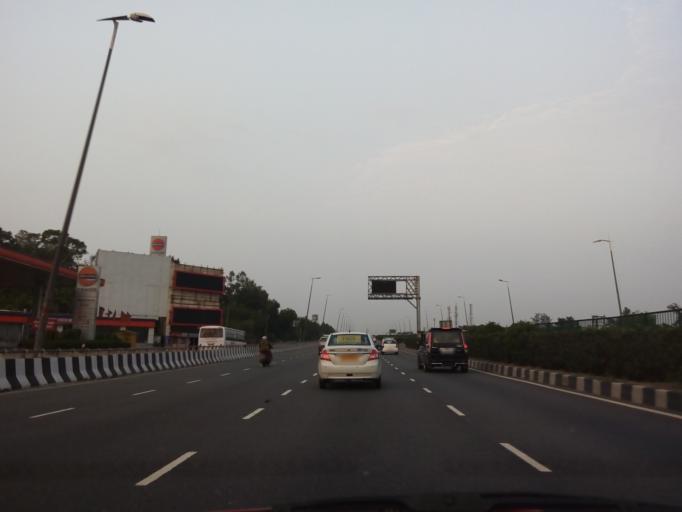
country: IN
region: Haryana
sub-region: Gurgaon
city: Gurgaon
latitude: 28.5255
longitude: 77.1009
